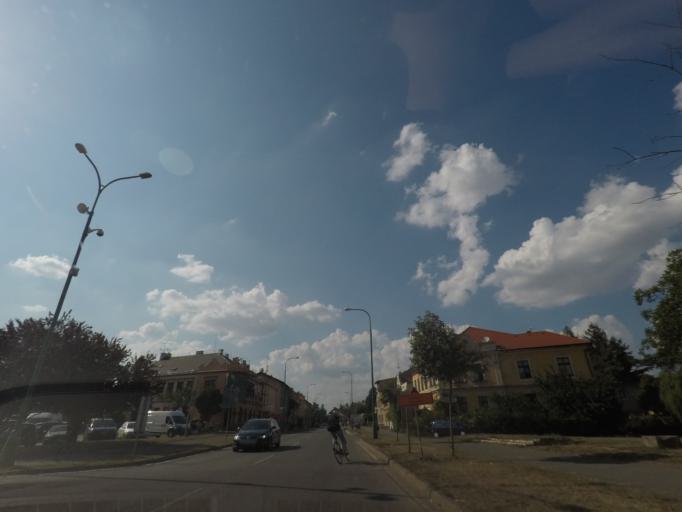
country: CZ
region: Kralovehradecky
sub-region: Okres Nachod
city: Jaromer
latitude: 50.3460
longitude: 15.9168
